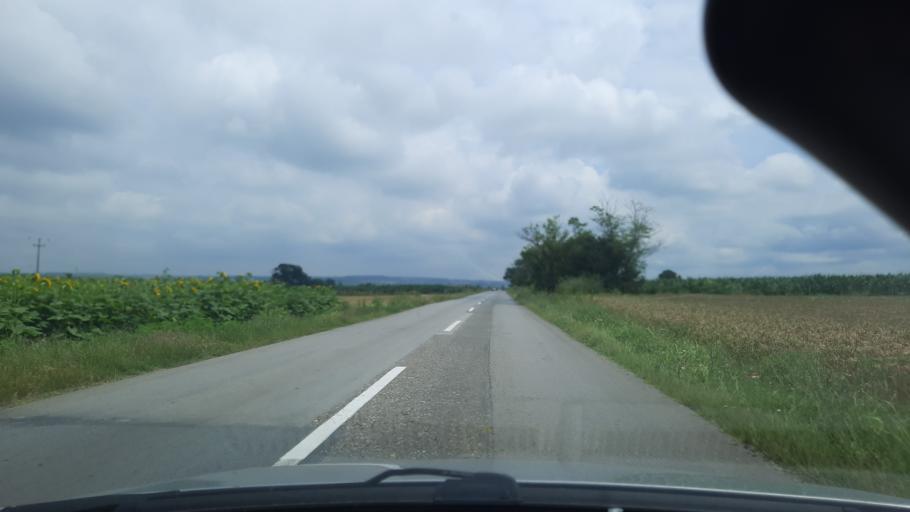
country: RS
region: Central Serbia
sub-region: Branicevski Okrug
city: Malo Crnice
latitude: 44.5828
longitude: 21.3050
